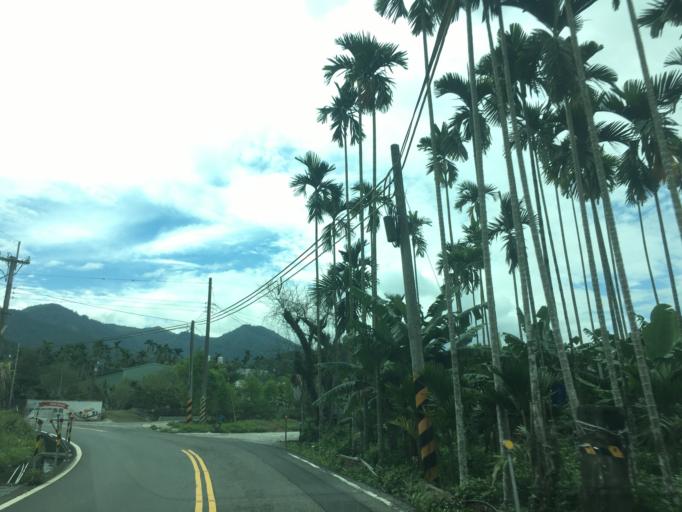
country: TW
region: Taiwan
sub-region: Yunlin
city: Douliu
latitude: 23.5677
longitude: 120.5681
